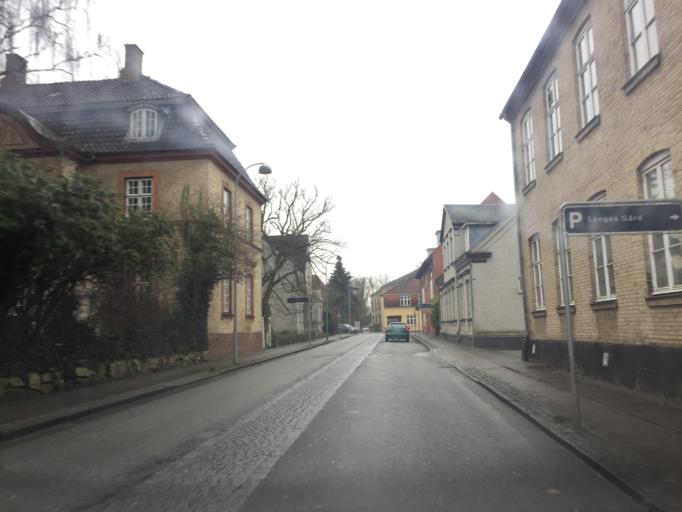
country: DK
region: Zealand
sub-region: Slagelse Kommune
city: Slagelse
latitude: 55.4043
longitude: 11.3582
